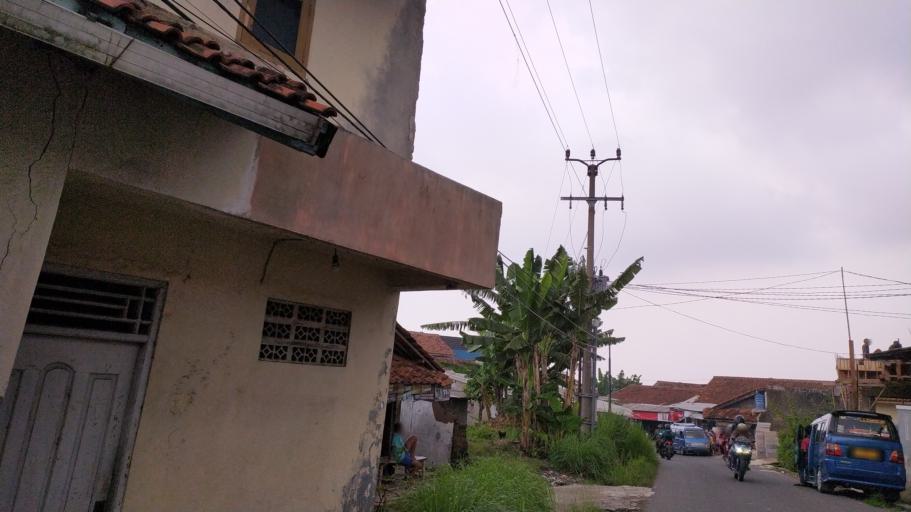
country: ID
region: West Java
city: Ciampea
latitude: -6.6130
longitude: 106.6968
